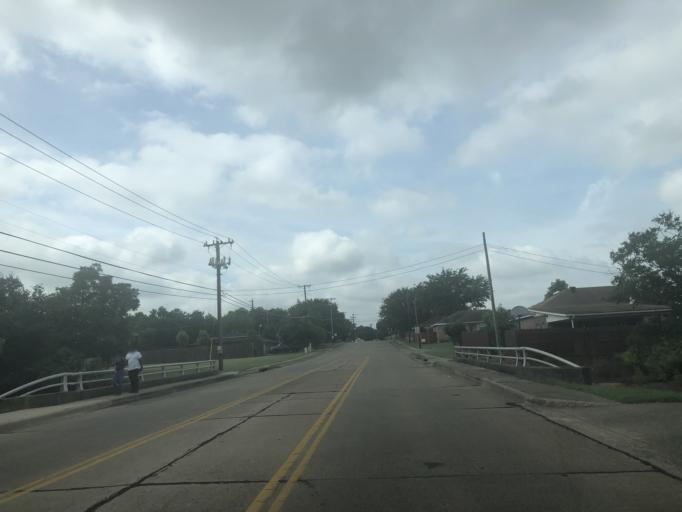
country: US
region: Texas
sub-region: Dallas County
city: Irving
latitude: 32.8041
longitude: -96.9631
